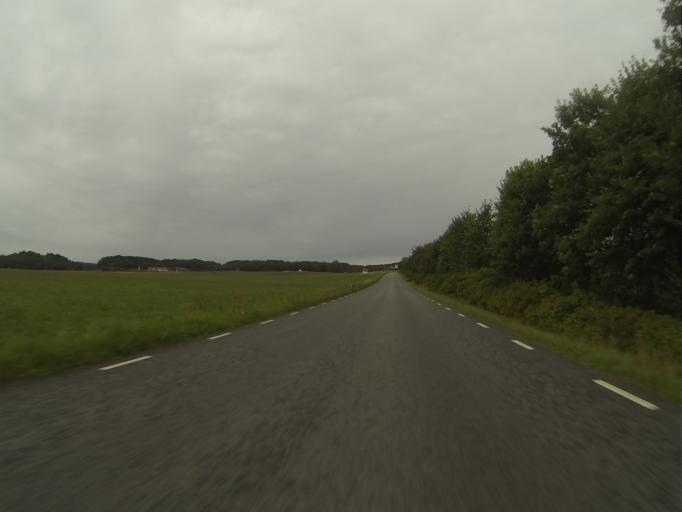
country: SE
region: Skane
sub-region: Lunds Kommun
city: Veberod
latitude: 55.6738
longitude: 13.4303
